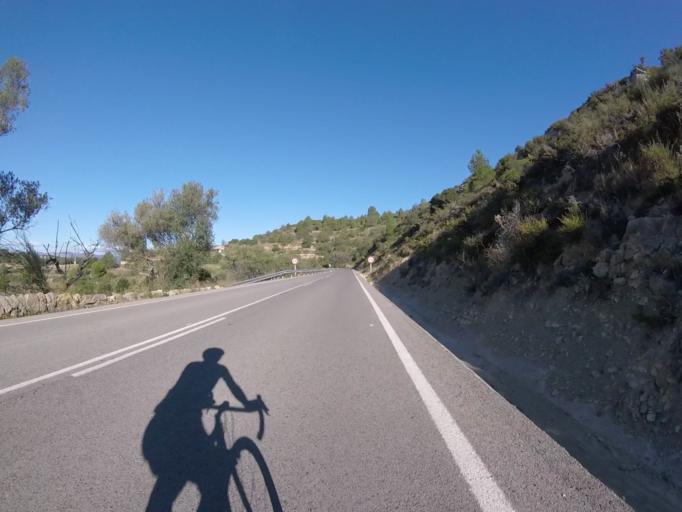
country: ES
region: Valencia
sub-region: Provincia de Castello
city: Cervera del Maestre
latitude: 40.4571
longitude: 0.2659
